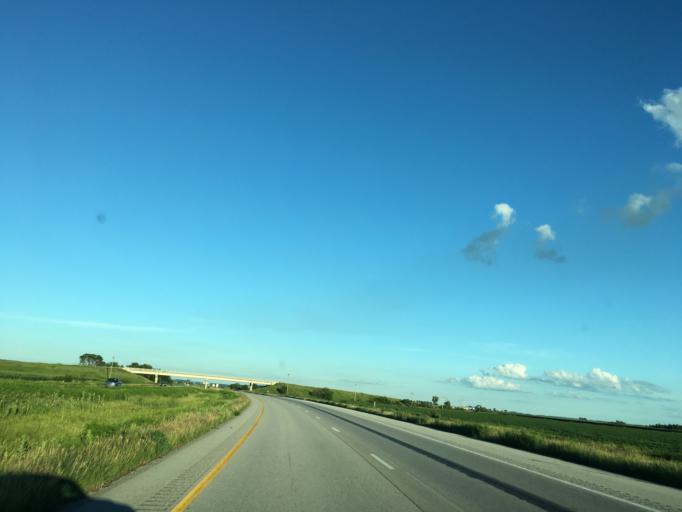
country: US
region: Iowa
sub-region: Fremont County
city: Hamburg
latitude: 40.6419
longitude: -95.7401
